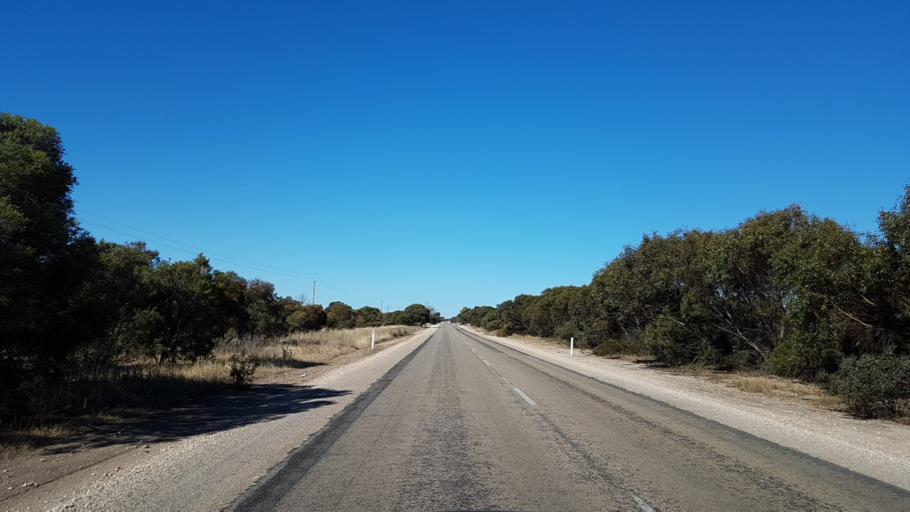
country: AU
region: South Australia
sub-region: Yorke Peninsula
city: Honiton
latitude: -34.8434
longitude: 137.5242
